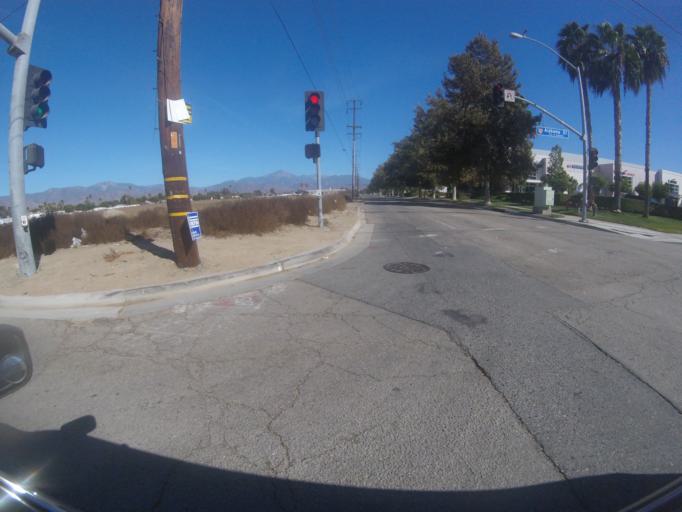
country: US
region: California
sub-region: San Bernardino County
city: Redlands
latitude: 34.0593
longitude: -117.2088
